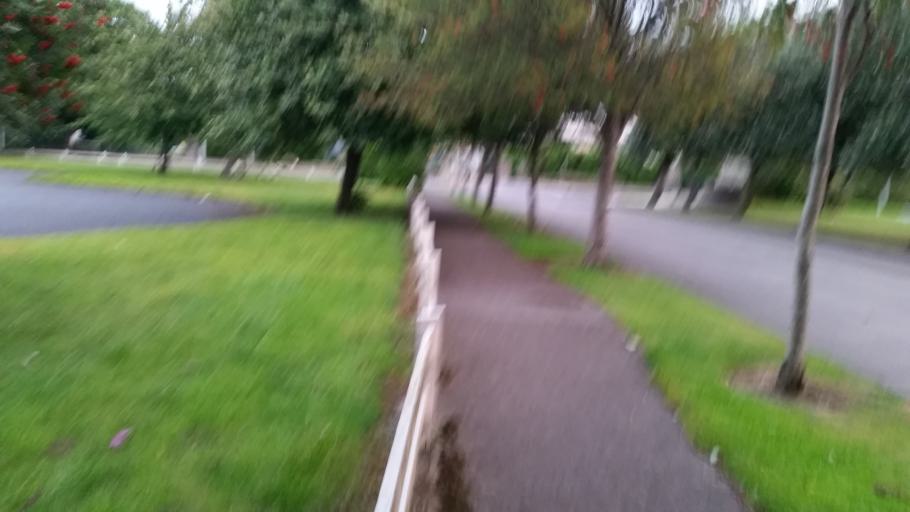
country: IE
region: Leinster
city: Beaumont
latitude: 53.4069
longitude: -6.2350
